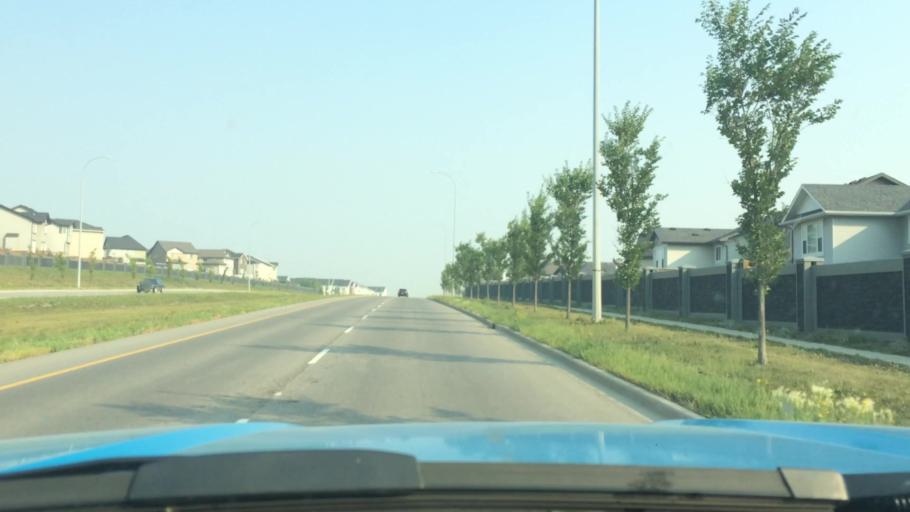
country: CA
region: Alberta
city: Calgary
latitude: 51.1771
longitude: -114.1578
